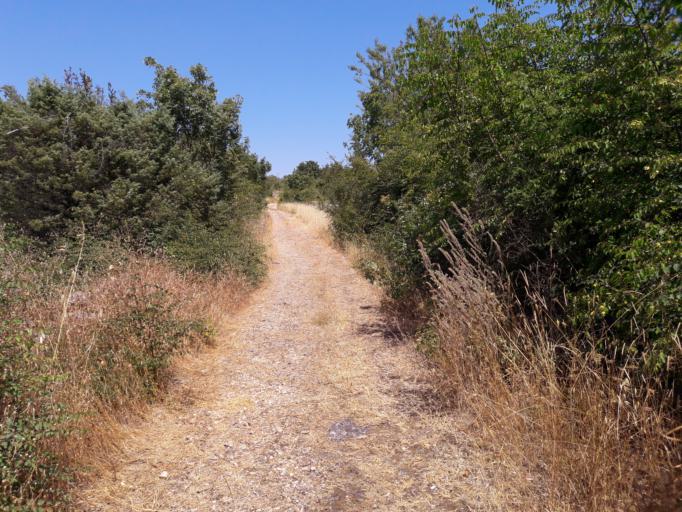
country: HR
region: Sibensko-Kniniska
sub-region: Grad Sibenik
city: Sibenik
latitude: 43.6910
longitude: 15.8509
